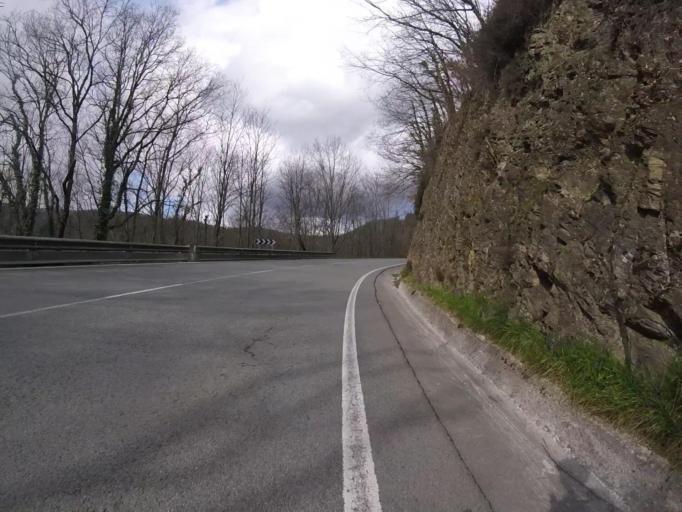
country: ES
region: Navarre
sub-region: Provincia de Navarra
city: Etxalar
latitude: 43.2354
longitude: -1.6511
